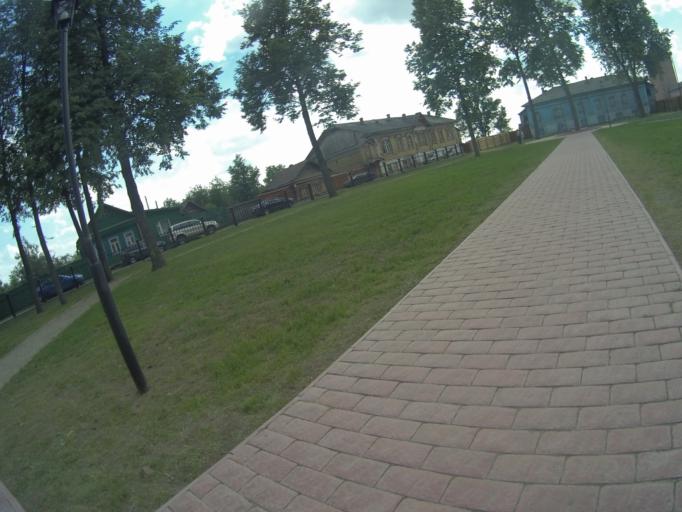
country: RU
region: Vladimir
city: Suzdal'
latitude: 56.4318
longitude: 40.4425
